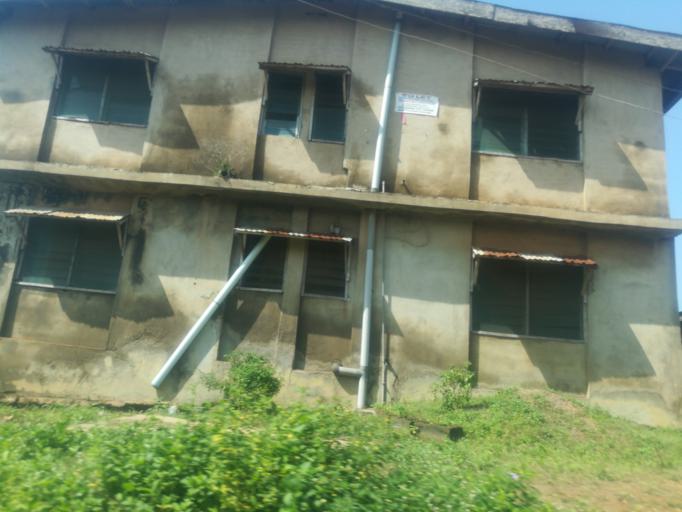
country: NG
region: Oyo
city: Egbeda
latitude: 7.4216
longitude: 3.9838
